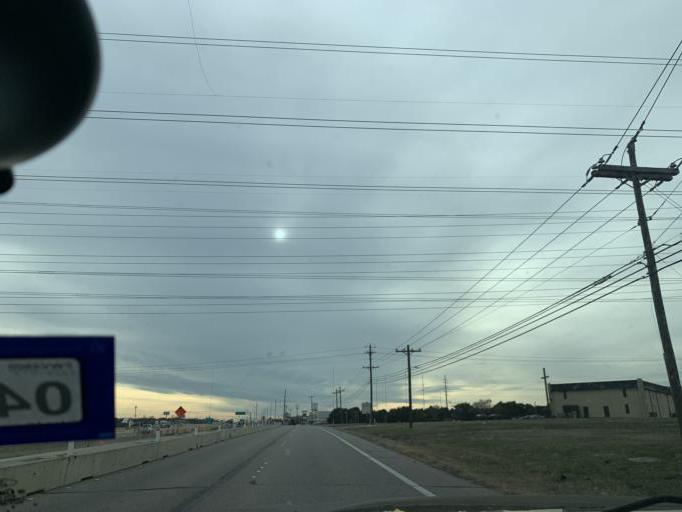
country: US
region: Texas
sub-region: Dallas County
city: Shamrock
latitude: 32.6137
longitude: -96.9220
